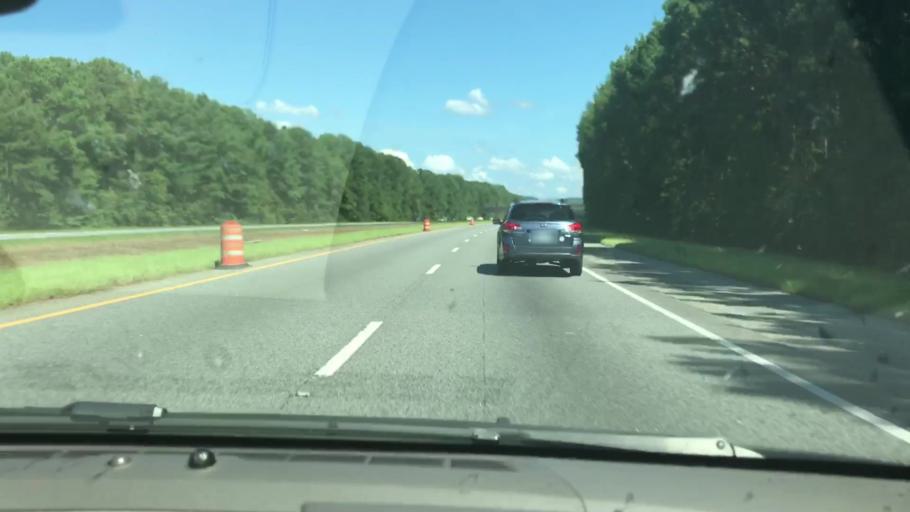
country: US
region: Georgia
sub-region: Harris County
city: Hamilton
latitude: 32.6743
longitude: -84.9882
